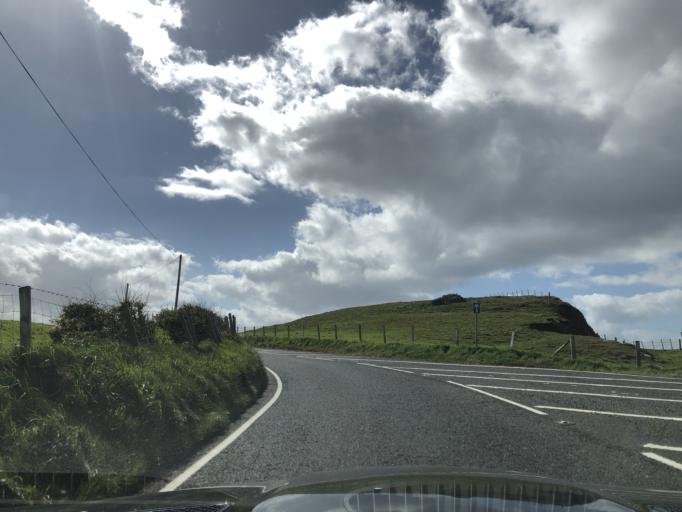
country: GB
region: Northern Ireland
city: Bushmills
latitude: 55.2127
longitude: -6.5722
